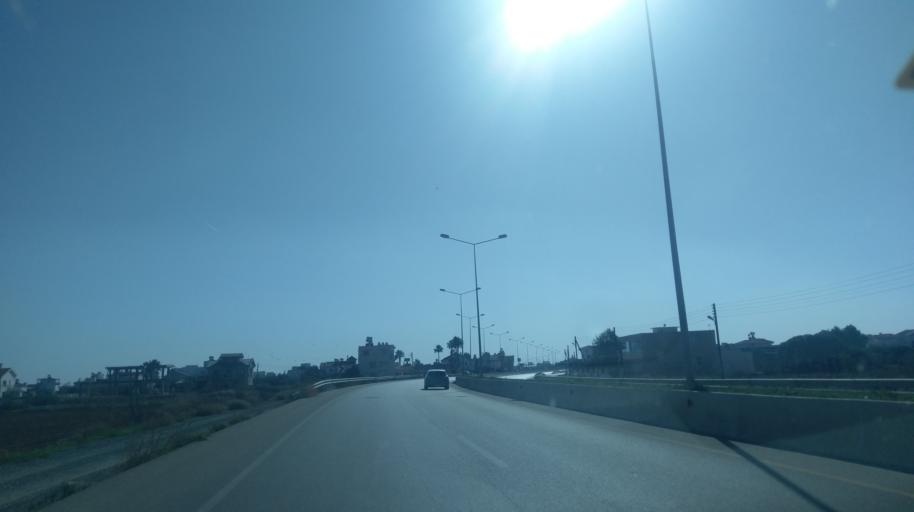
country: CY
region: Ammochostos
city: Trikomo
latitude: 35.2176
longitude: 33.8947
